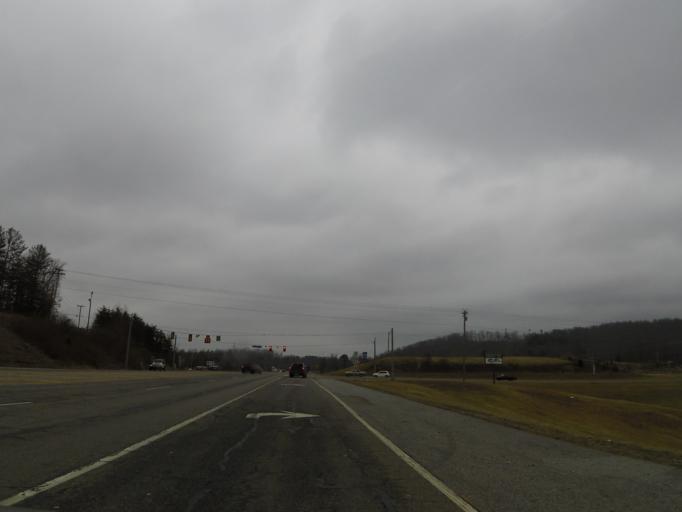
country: US
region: Tennessee
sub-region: Scott County
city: Huntsville
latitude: 36.4115
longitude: -84.5377
